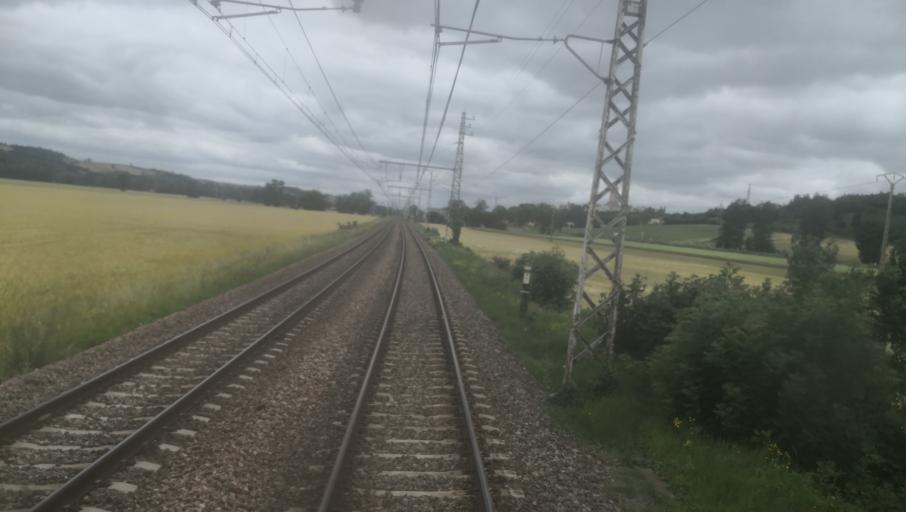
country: FR
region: Midi-Pyrenees
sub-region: Departement de la Haute-Garonne
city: Avignonet-Lauragais
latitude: 43.3608
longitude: 1.7995
